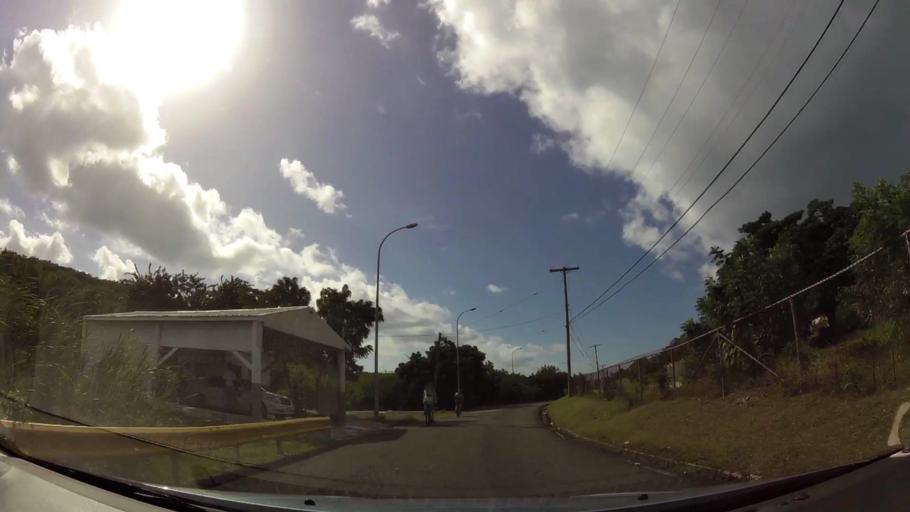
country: AG
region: Saint John
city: Saint John's
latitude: 17.1190
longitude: -61.8839
